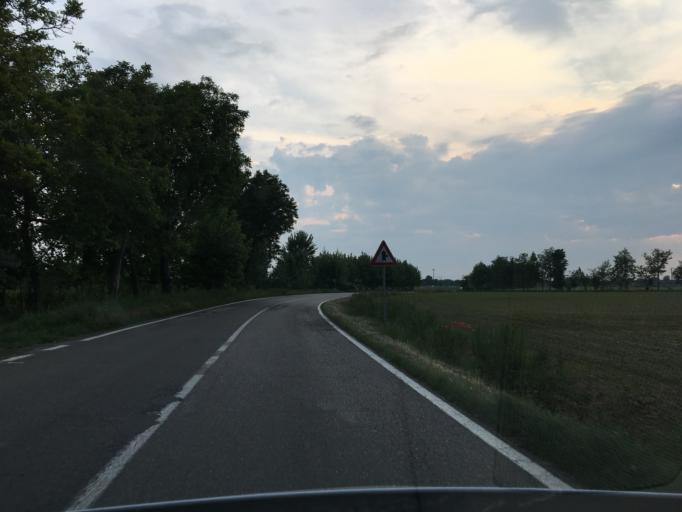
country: IT
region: Lombardy
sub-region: Provincia di Brescia
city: Alfianello
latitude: 45.2704
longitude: 10.1715
